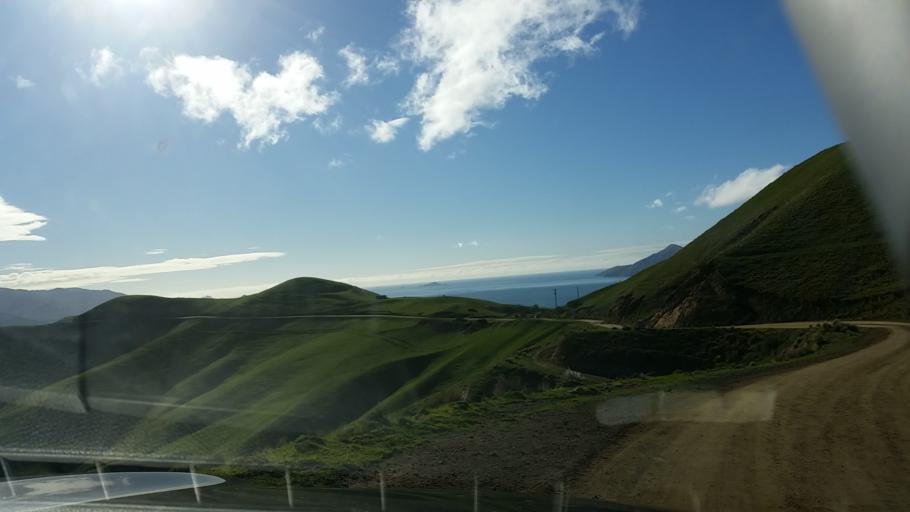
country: NZ
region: Marlborough
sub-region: Marlborough District
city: Picton
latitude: -40.9511
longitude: 173.8335
